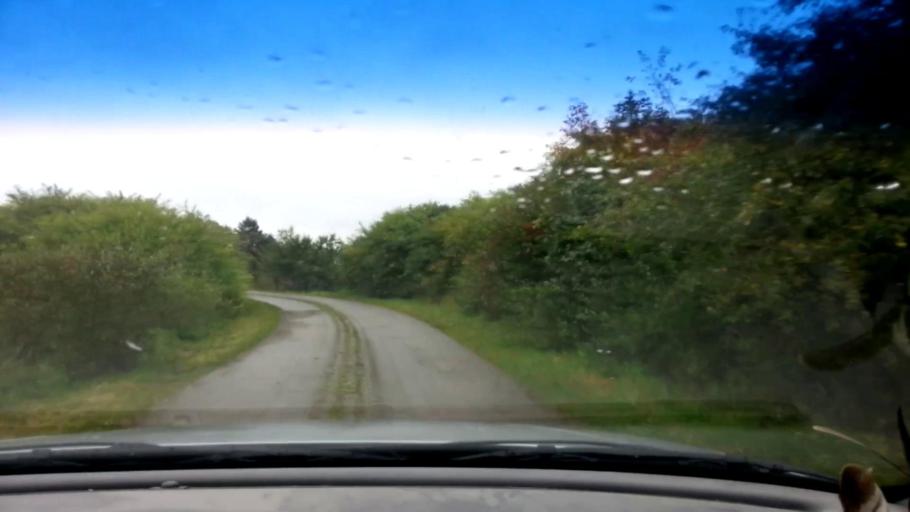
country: DE
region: Bavaria
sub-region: Upper Franconia
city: Poxdorf
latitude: 49.9492
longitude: 11.0871
